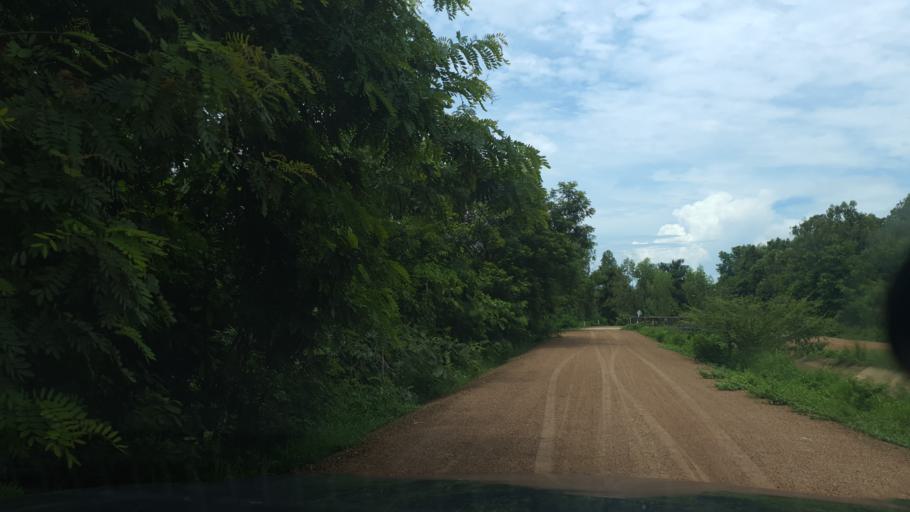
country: TH
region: Lampang
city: Hang Chat
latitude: 18.2793
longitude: 99.3729
